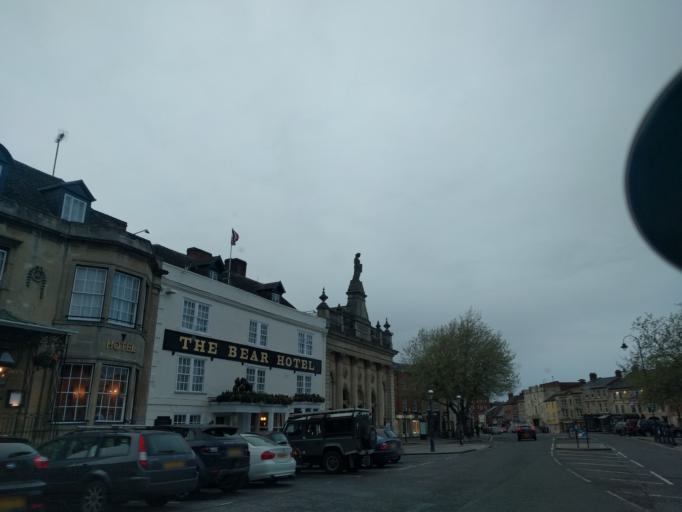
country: GB
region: England
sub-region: Wiltshire
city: Devizes
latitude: 51.3522
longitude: -1.9955
